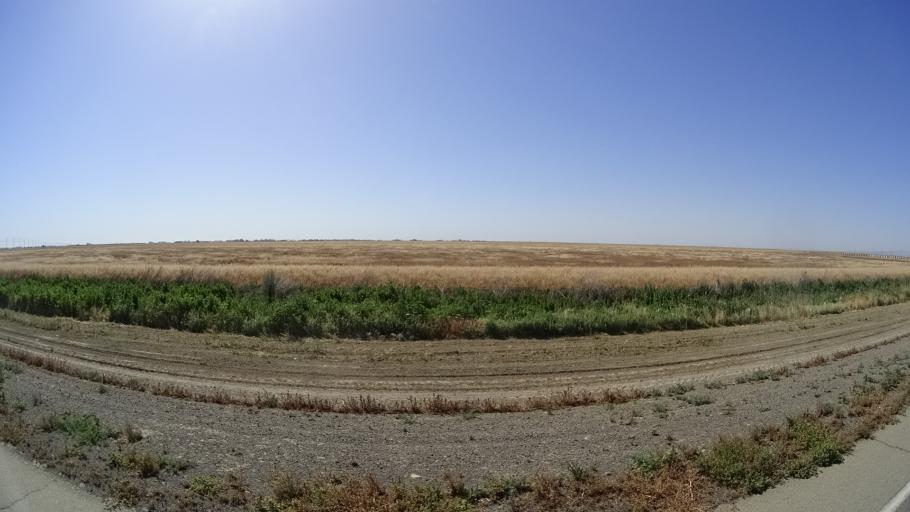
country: US
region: California
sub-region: Kings County
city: Lemoore Station
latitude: 36.2246
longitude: -119.9003
